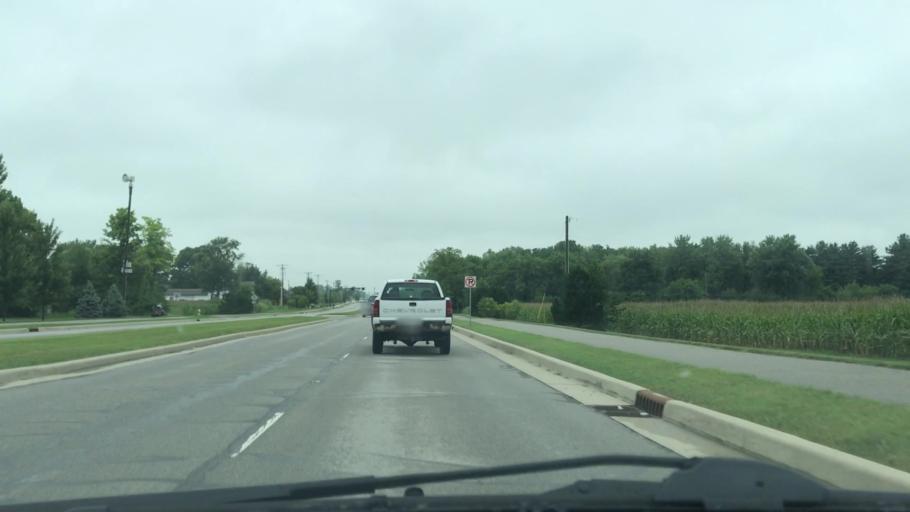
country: US
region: Indiana
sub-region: Hamilton County
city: Westfield
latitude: 40.0375
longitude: -86.0706
